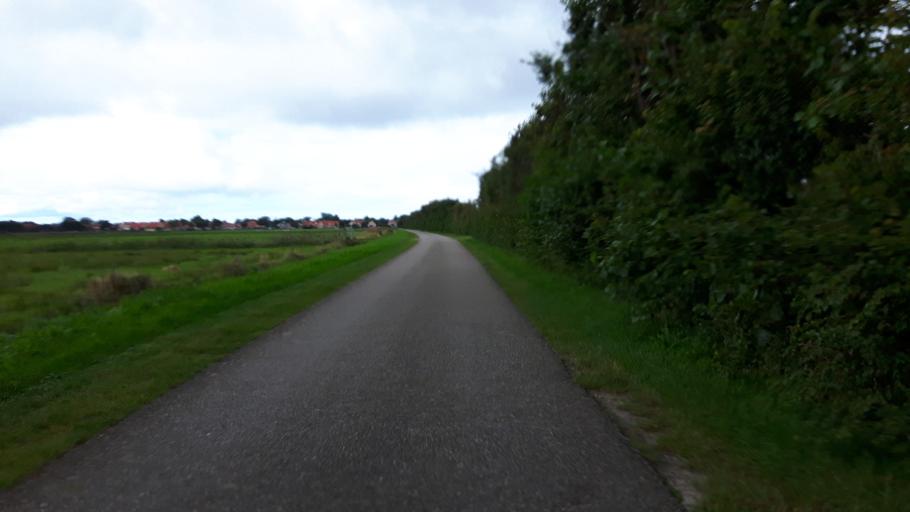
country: NL
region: Friesland
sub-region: Gemeente Ameland
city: Hollum
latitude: 53.4420
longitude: 5.6541
